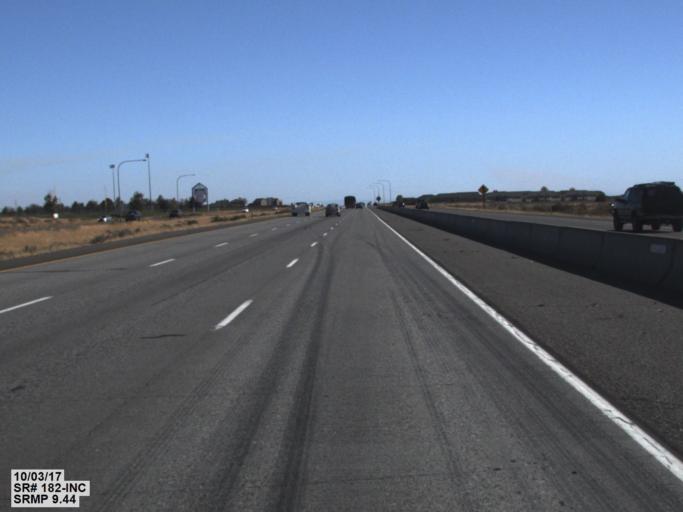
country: US
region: Washington
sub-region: Franklin County
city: West Pasco
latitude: 46.2648
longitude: -119.1803
